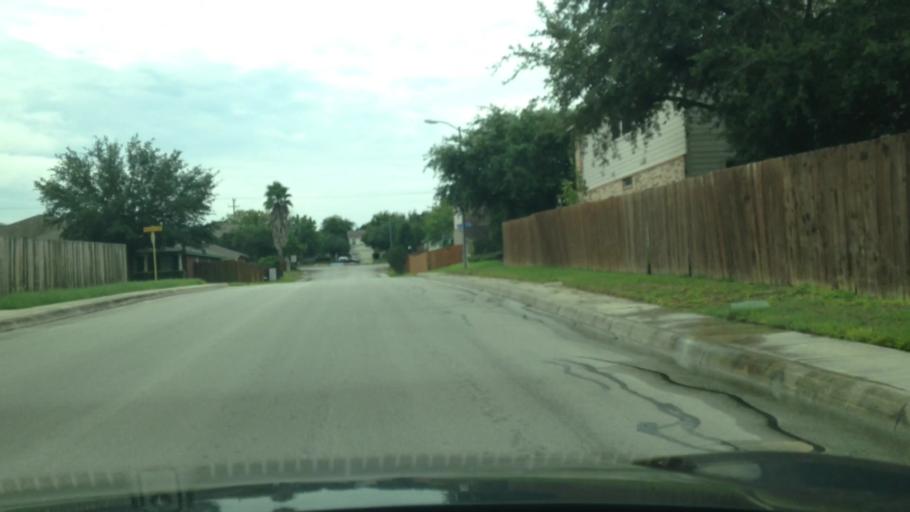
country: US
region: Texas
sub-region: Bexar County
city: Live Oak
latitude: 29.5860
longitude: -98.3837
